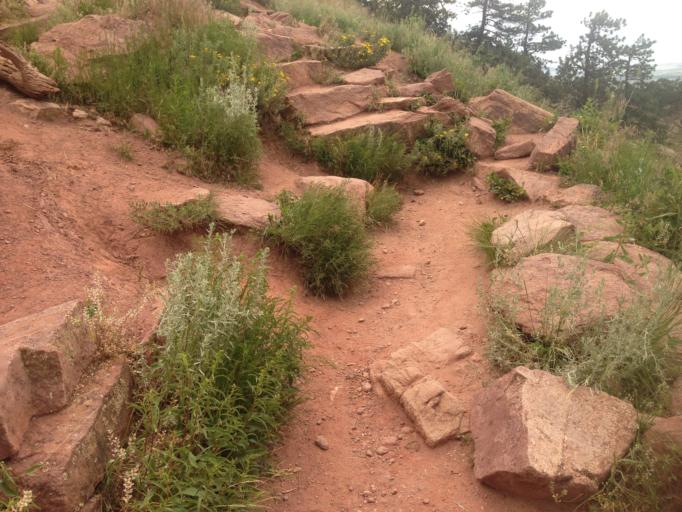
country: US
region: Colorado
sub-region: Boulder County
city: Boulder
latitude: 40.0284
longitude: -105.3021
